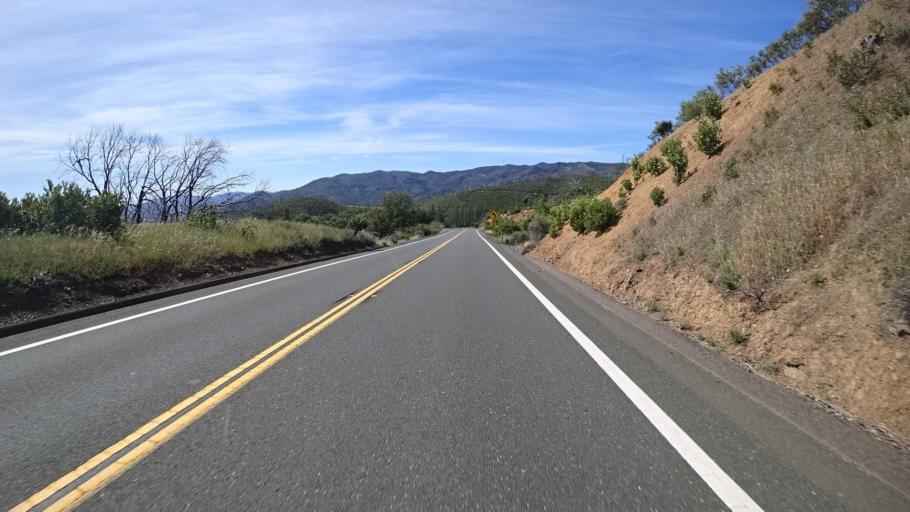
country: US
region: California
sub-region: Lake County
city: Cobb
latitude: 38.7966
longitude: -122.7038
